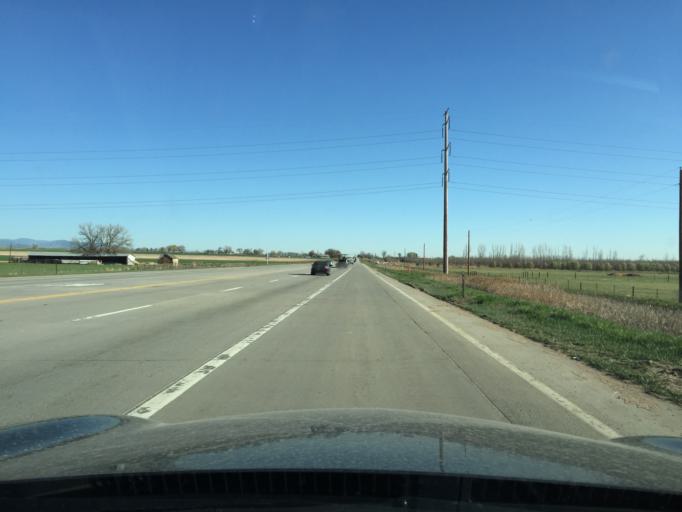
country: US
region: Colorado
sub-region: Boulder County
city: Erie
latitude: 40.0734
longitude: -105.1024
